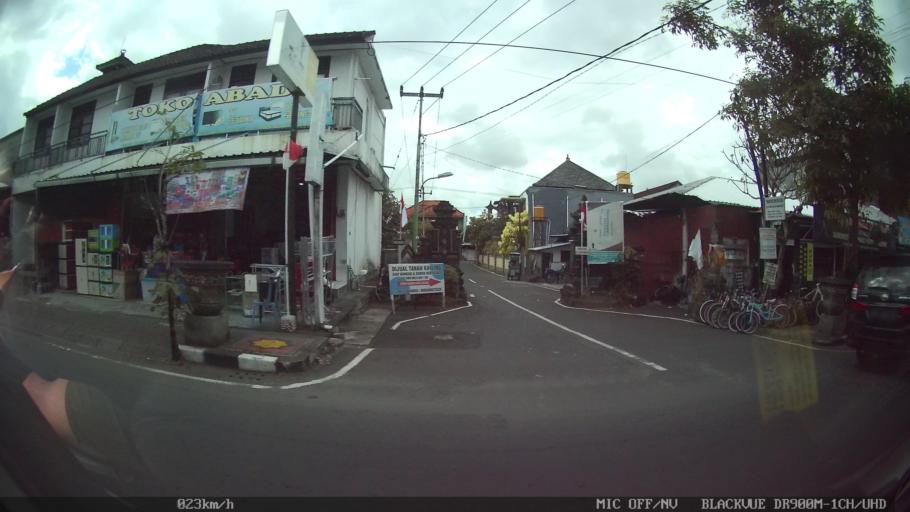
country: ID
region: Bali
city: Banjar Karangsuling
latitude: -8.6057
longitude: 115.1712
